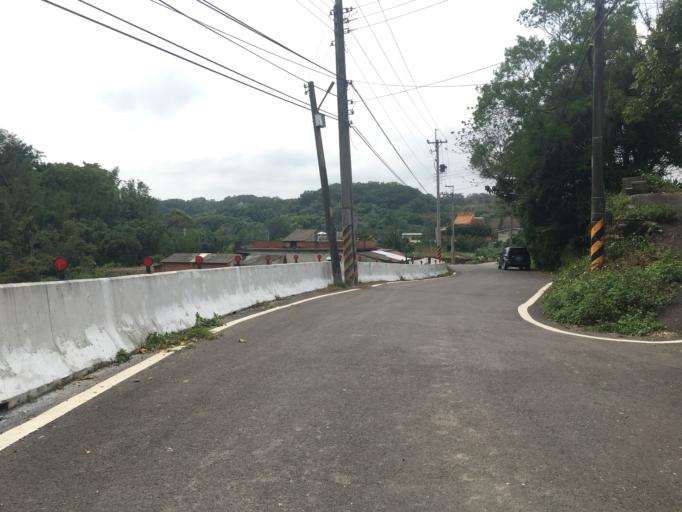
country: TW
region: Taiwan
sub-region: Hsinchu
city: Hsinchu
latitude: 24.7375
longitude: 120.9757
